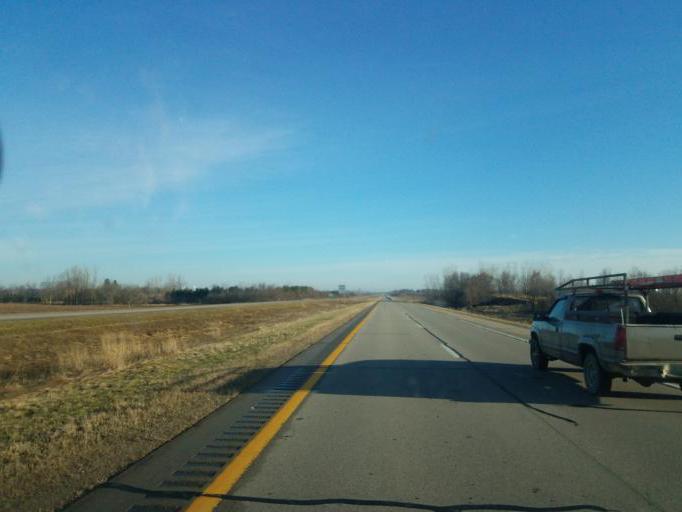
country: US
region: Michigan
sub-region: Clinton County
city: Saint Johns
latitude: 42.9472
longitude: -84.5185
